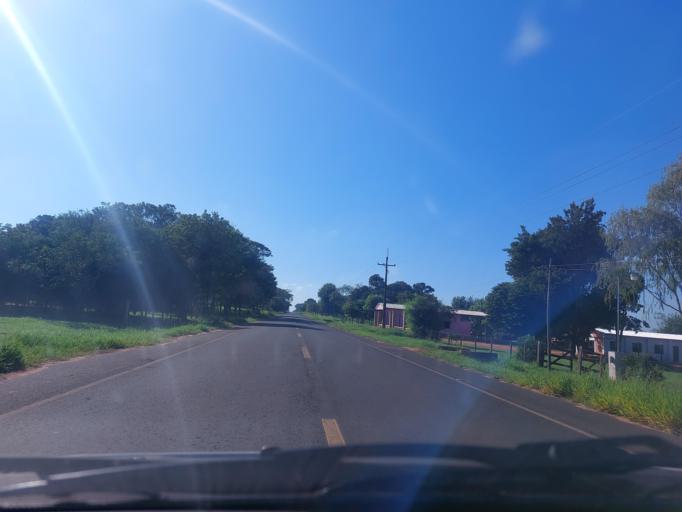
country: PY
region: San Pedro
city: Guayaybi
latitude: -24.5320
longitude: -56.5082
